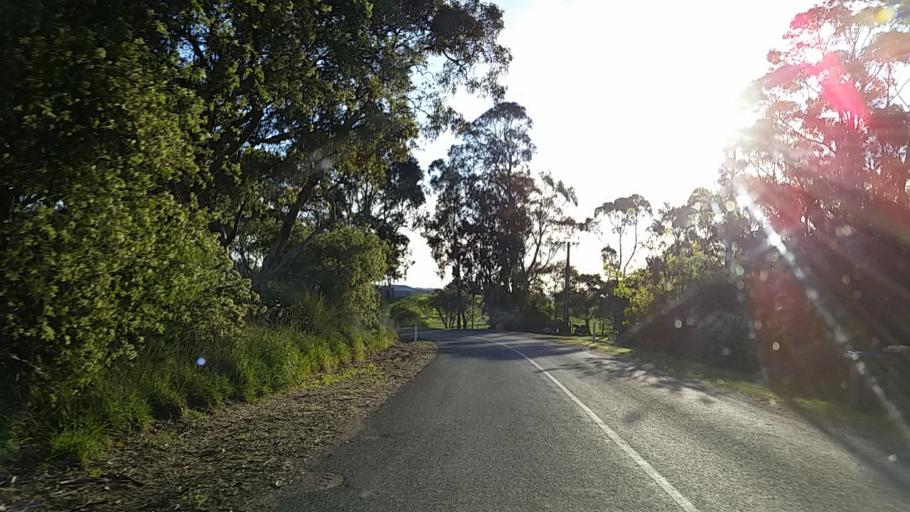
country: AU
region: South Australia
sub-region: Mount Barker
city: Meadows
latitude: -35.2252
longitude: 138.7303
